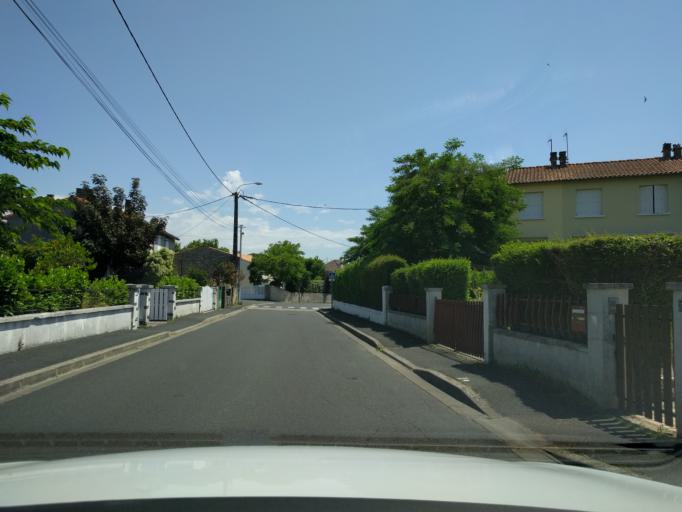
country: FR
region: Poitou-Charentes
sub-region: Departement des Deux-Sevres
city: Niort
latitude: 46.3483
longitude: -0.4728
